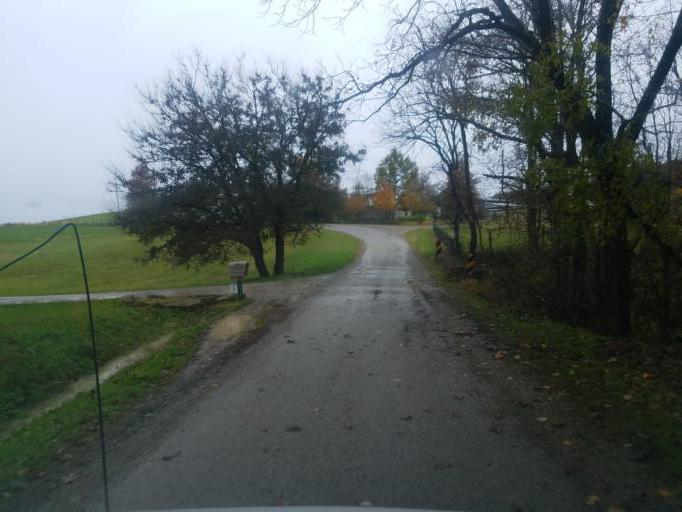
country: US
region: Ohio
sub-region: Washington County
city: Beverly
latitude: 39.4704
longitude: -81.6863
